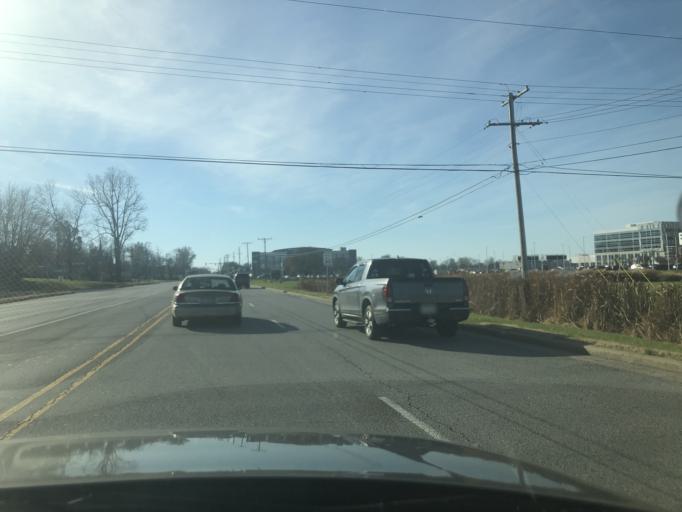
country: US
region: Indiana
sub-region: Warrick County
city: Newburgh
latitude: 37.9764
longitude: -87.4413
